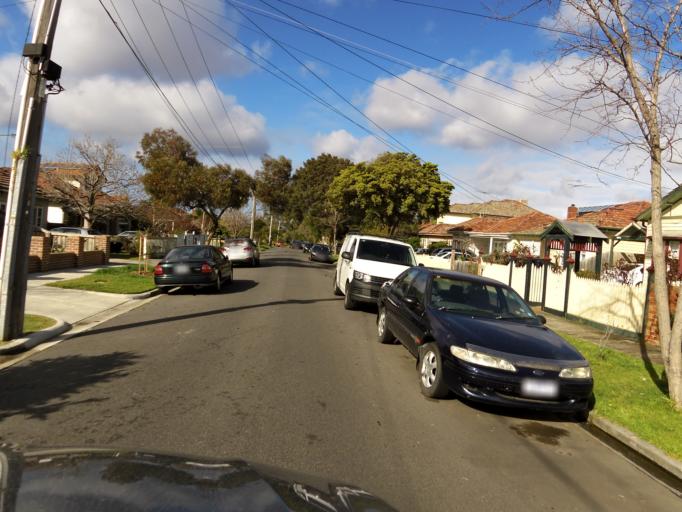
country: AU
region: Victoria
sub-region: Maribyrnong
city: Kingsville
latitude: -37.8130
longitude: 144.8759
